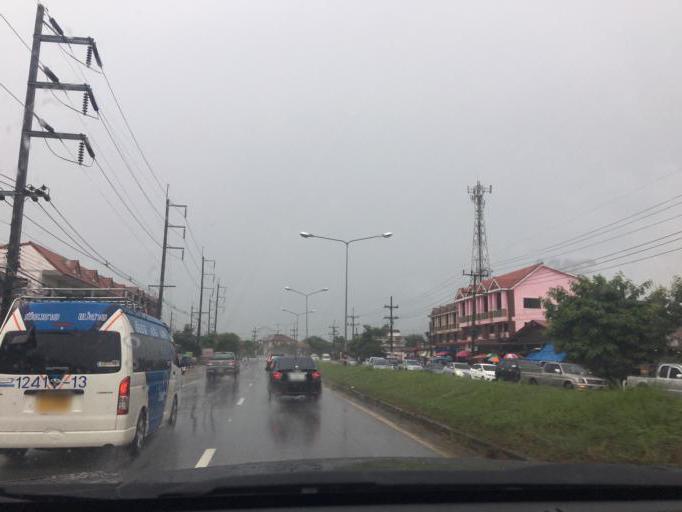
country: TH
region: Chiang Rai
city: Mae Fa Luang
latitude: 20.2632
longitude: 99.8573
